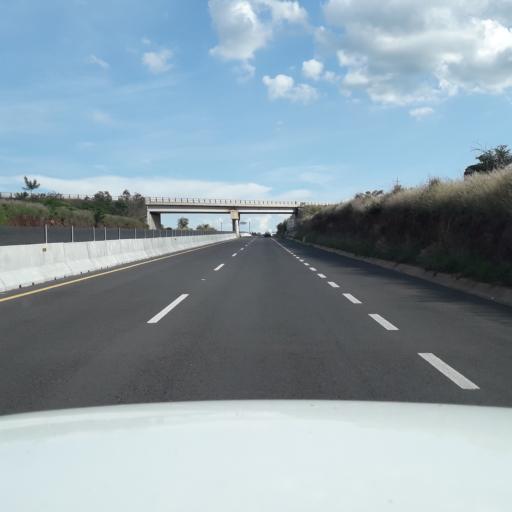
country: MX
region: Jalisco
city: Arenal
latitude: 20.7887
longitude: -103.7129
